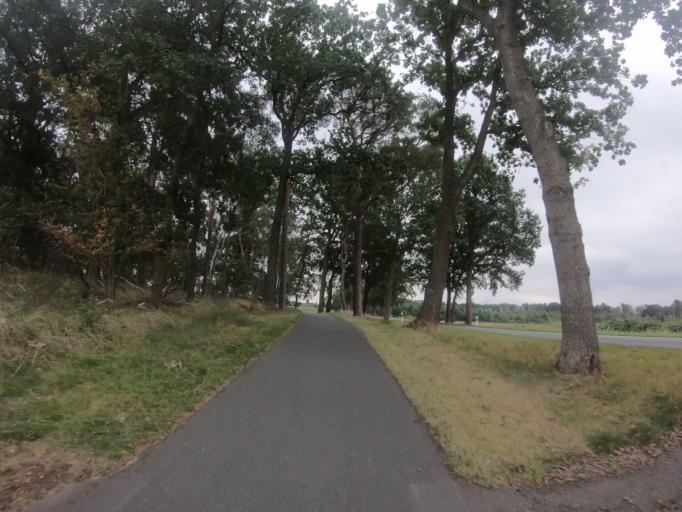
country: DE
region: Lower Saxony
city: Ribbesbuttel
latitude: 52.4401
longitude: 10.5040
